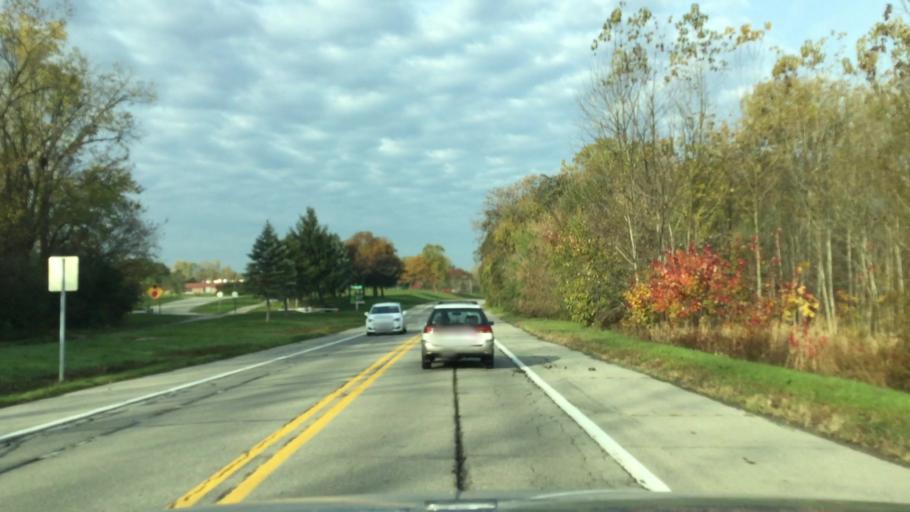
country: US
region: Michigan
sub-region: Wayne County
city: Dearborn Heights
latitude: 42.3447
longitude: -83.2674
